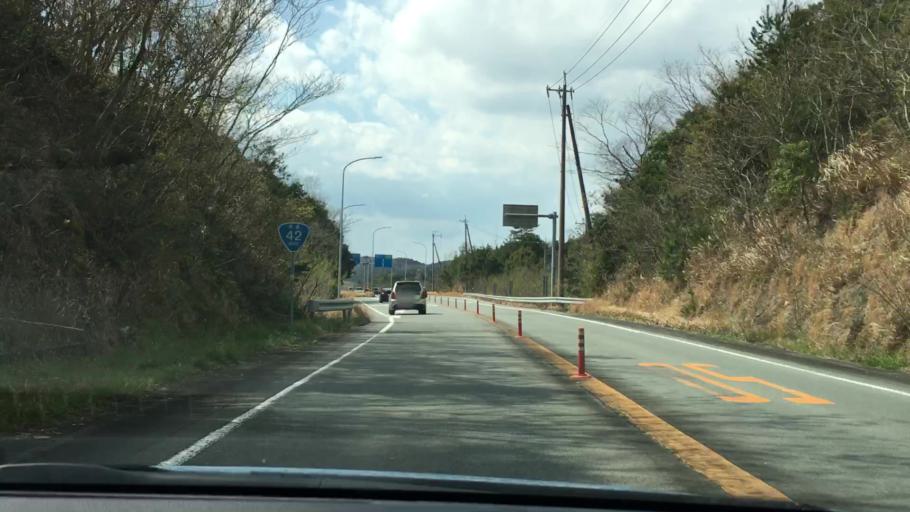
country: JP
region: Mie
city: Toba
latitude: 34.4932
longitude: 136.7844
